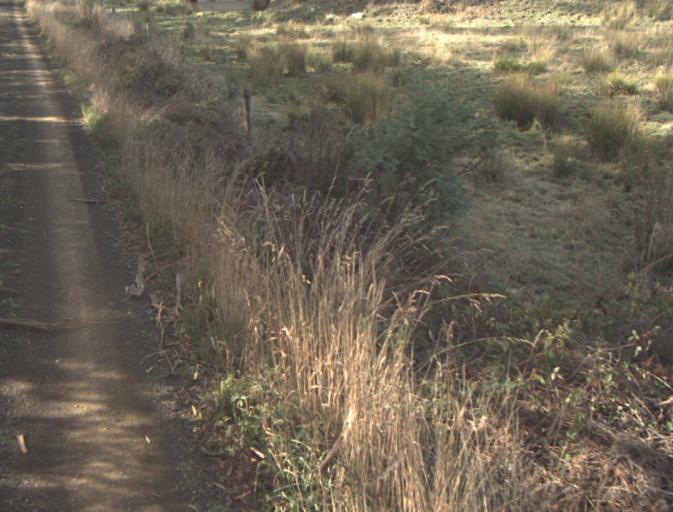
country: AU
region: Tasmania
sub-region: Launceston
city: Mayfield
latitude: -41.2096
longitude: 147.1499
